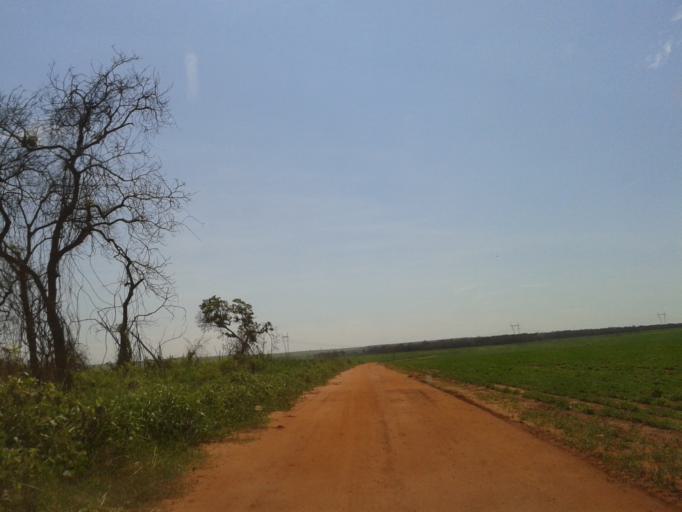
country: BR
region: Minas Gerais
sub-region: Santa Vitoria
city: Santa Vitoria
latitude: -19.0643
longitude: -50.4757
